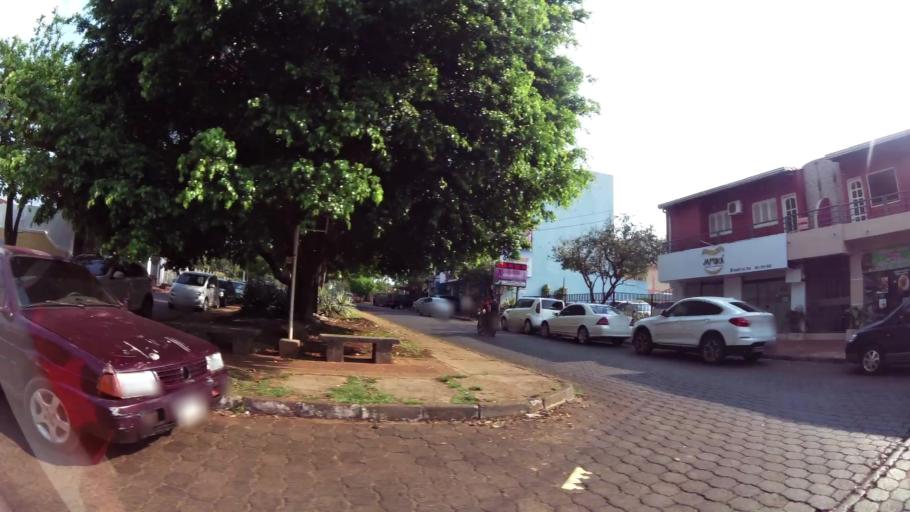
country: PY
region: Alto Parana
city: Presidente Franco
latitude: -25.5314
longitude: -54.6269
